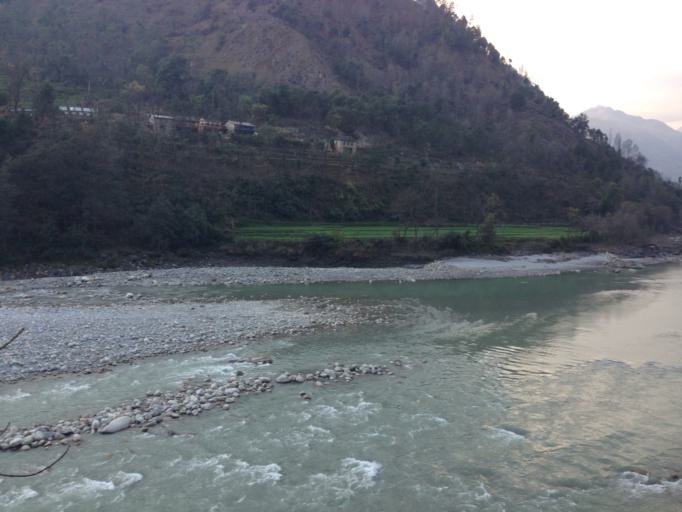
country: NP
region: Western Region
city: Baglung
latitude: 28.3070
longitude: 83.6020
